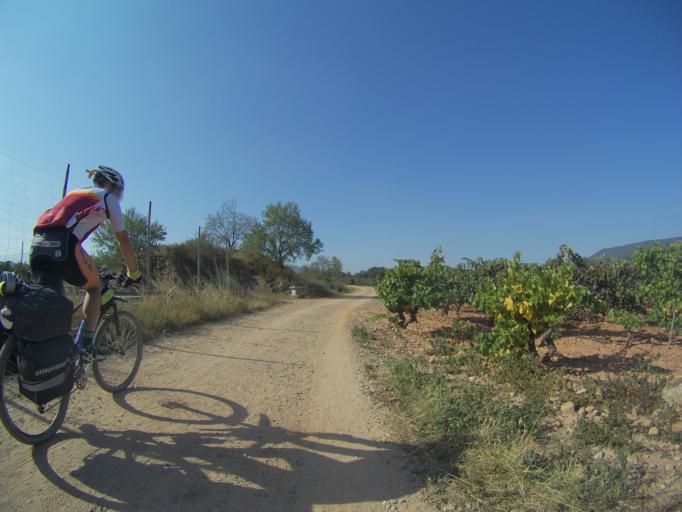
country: ES
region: La Rioja
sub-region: Provincia de La Rioja
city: Navarrete
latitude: 42.4192
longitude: -2.5838
